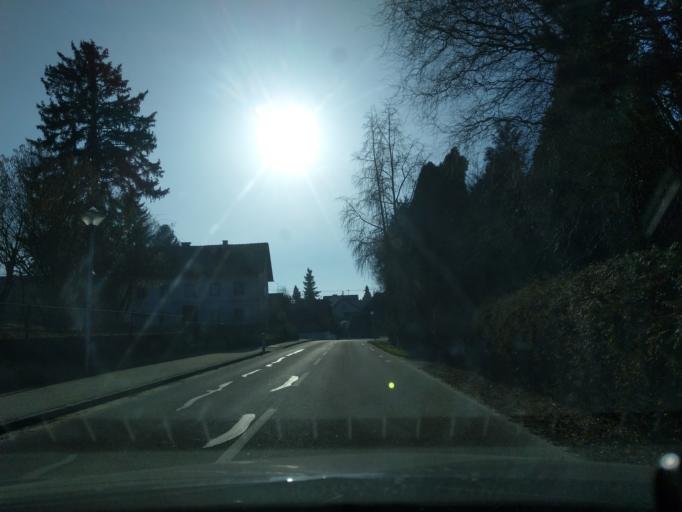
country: DE
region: Bavaria
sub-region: Lower Bavaria
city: Bad Fussing
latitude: 48.3337
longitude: 13.3621
